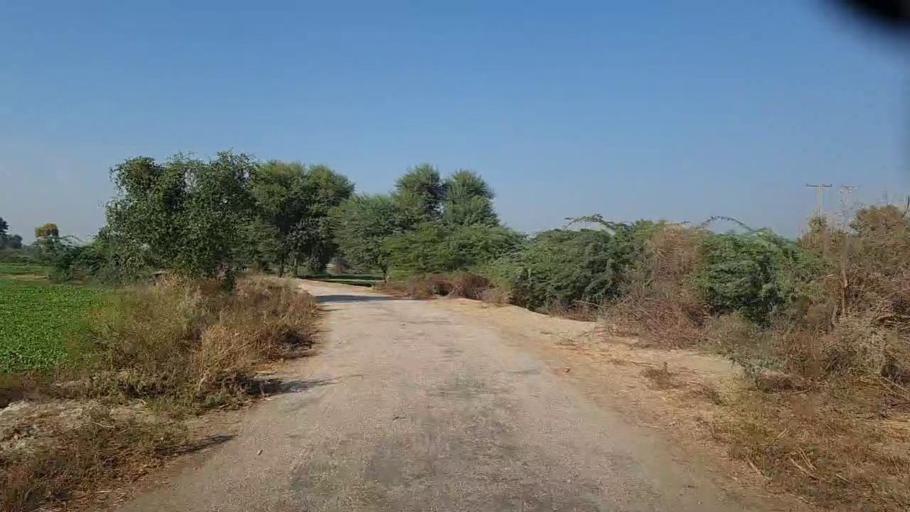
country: PK
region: Sindh
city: Darya Khan Marri
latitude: 26.6813
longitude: 68.3516
